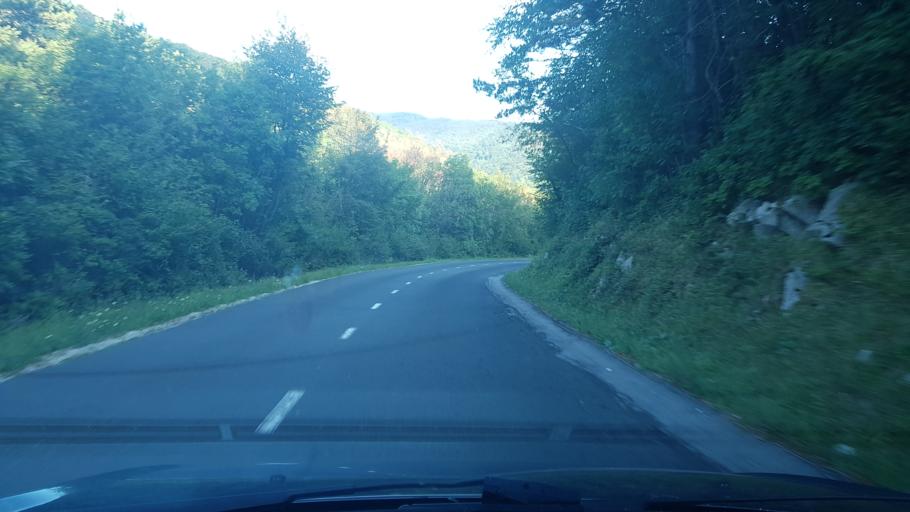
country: SI
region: Nova Gorica
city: Solkan
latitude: 46.0161
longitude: 13.6837
